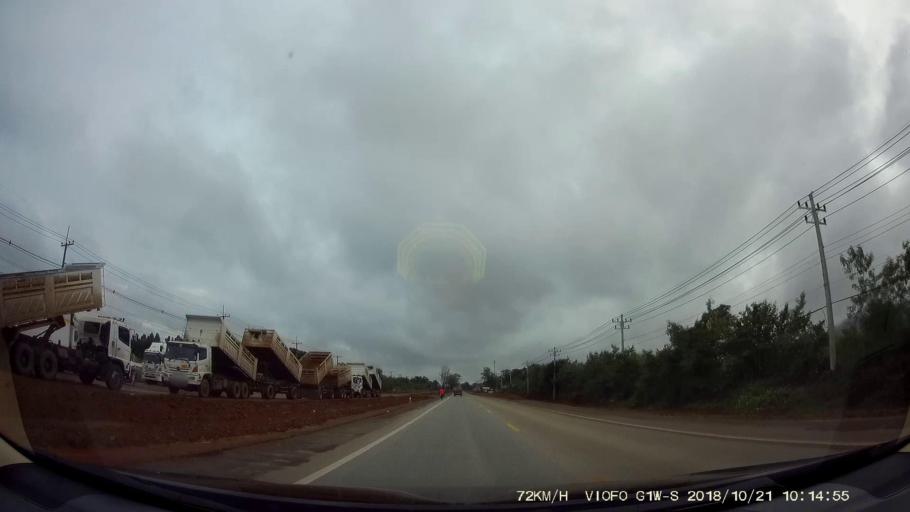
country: TH
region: Chaiyaphum
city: Phu Khiao
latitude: 16.3451
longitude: 102.1608
